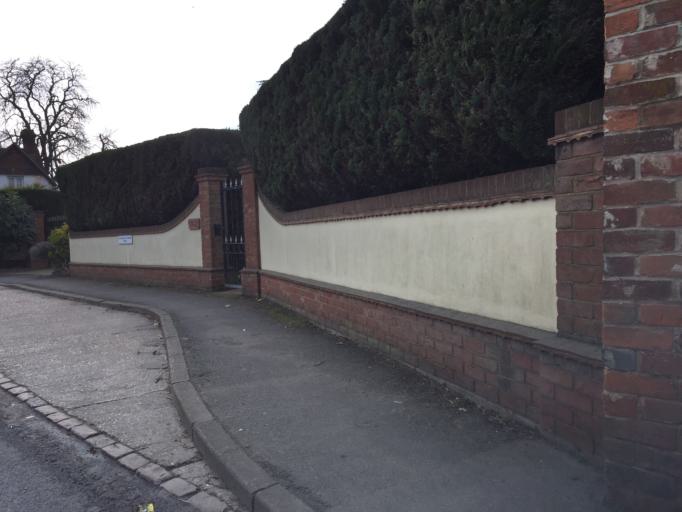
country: GB
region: England
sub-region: West Berkshire
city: Pangbourne
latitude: 51.4826
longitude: -1.0873
